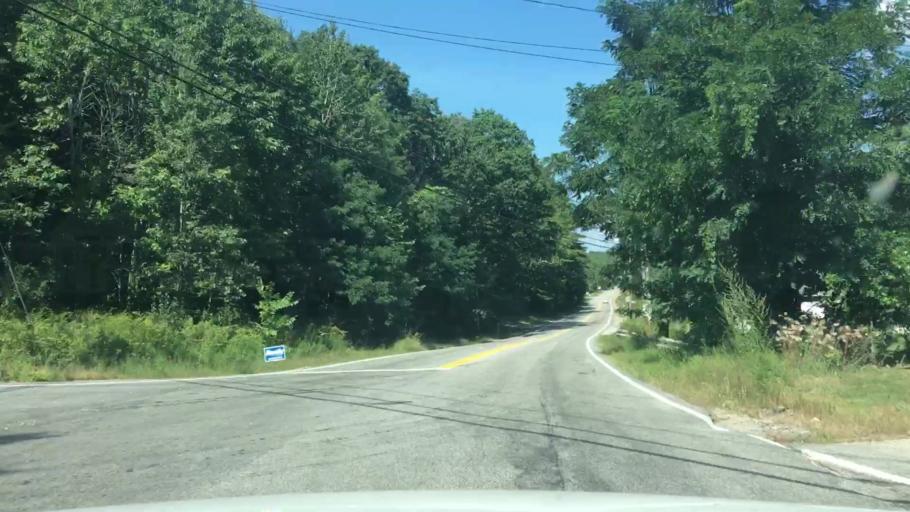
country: US
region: Maine
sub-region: Cumberland County
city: Falmouth
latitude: 43.7468
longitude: -70.2984
